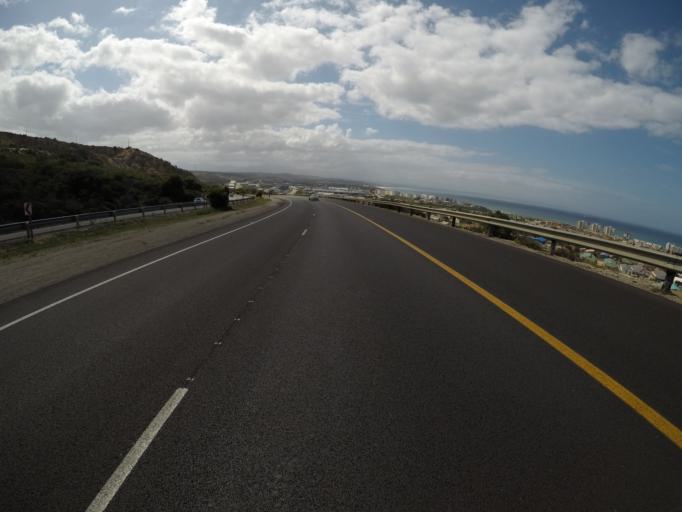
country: ZA
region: Western Cape
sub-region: Eden District Municipality
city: Mossel Bay
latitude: -34.1586
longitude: 22.0995
